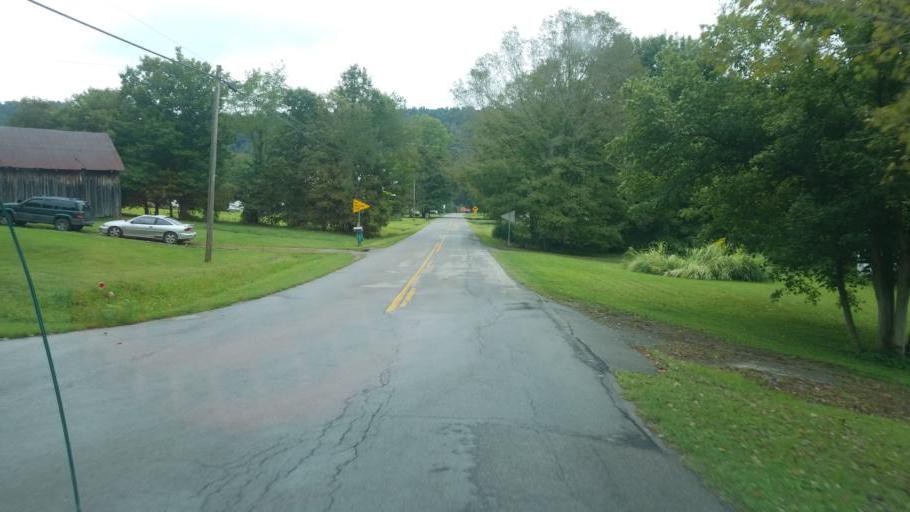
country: US
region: Kentucky
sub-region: Rowan County
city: Morehead
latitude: 38.3529
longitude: -83.5293
